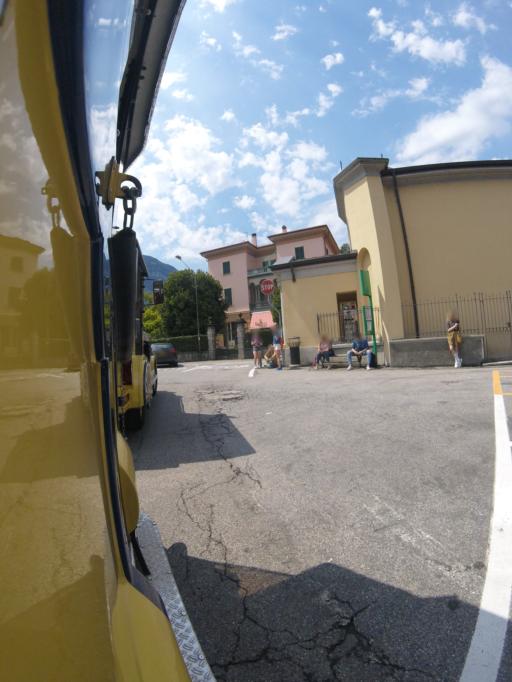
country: IT
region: Lombardy
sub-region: Provincia di Como
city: Griante
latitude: 46.0073
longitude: 9.2343
